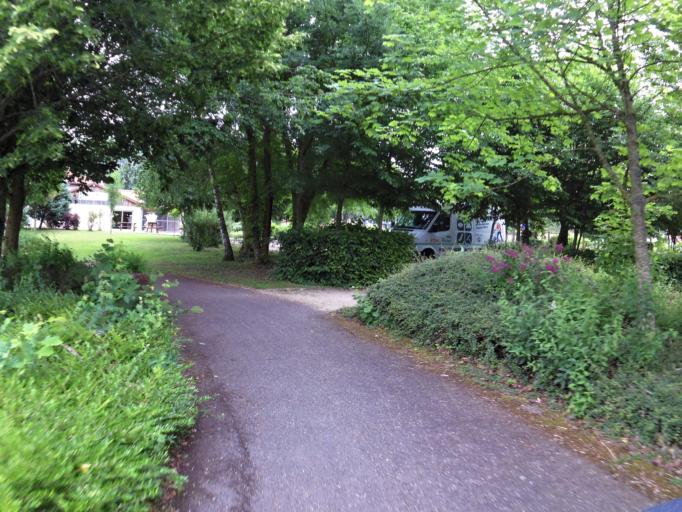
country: FR
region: Champagne-Ardenne
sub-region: Departement de la Haute-Marne
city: Montier-en-Der
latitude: 48.5526
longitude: 4.7748
